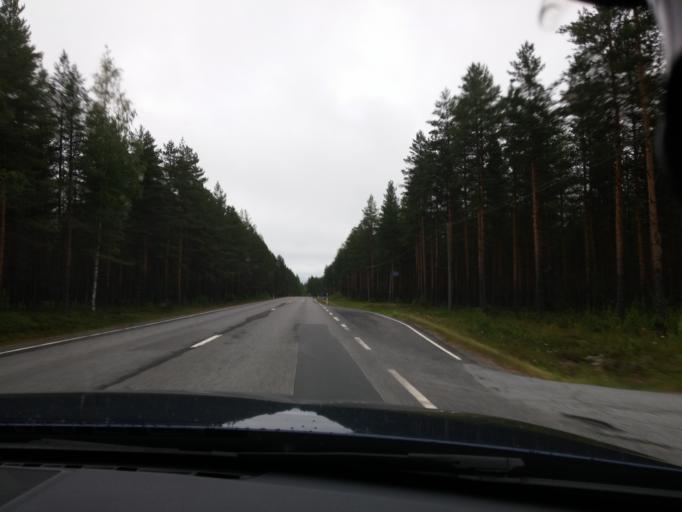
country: FI
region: Pirkanmaa
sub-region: Ylae-Pirkanmaa
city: Vilppula
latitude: 61.9424
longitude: 24.5416
